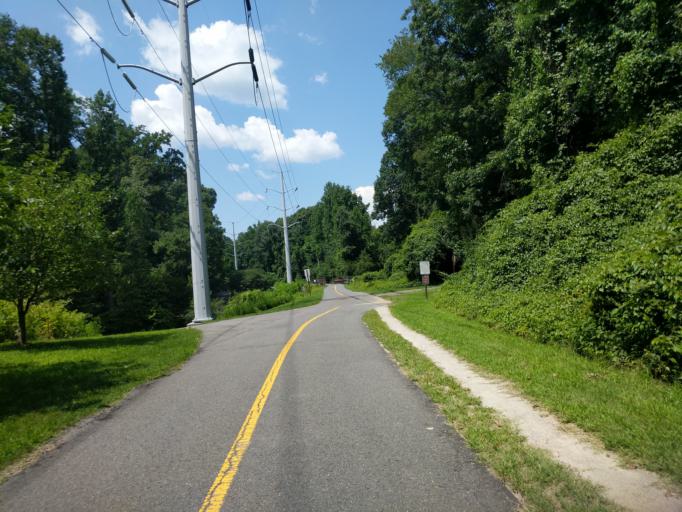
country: US
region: Virginia
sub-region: Fairfax County
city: Baileys Crossroads
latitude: 38.8633
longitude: -77.1180
